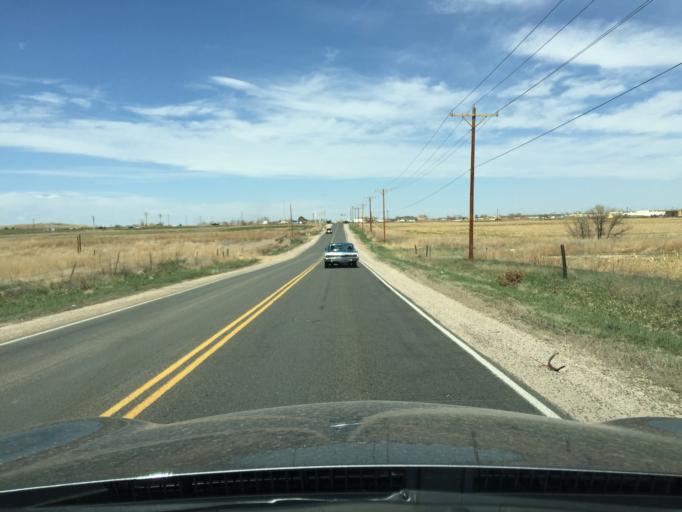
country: US
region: Colorado
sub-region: Boulder County
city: Erie
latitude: 39.9964
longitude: -104.9972
